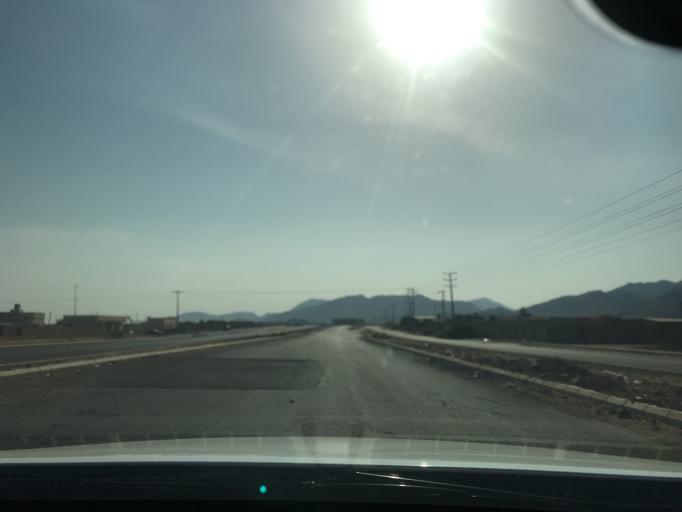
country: SA
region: Makkah
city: Al Jumum
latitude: 21.4540
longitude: 39.5413
